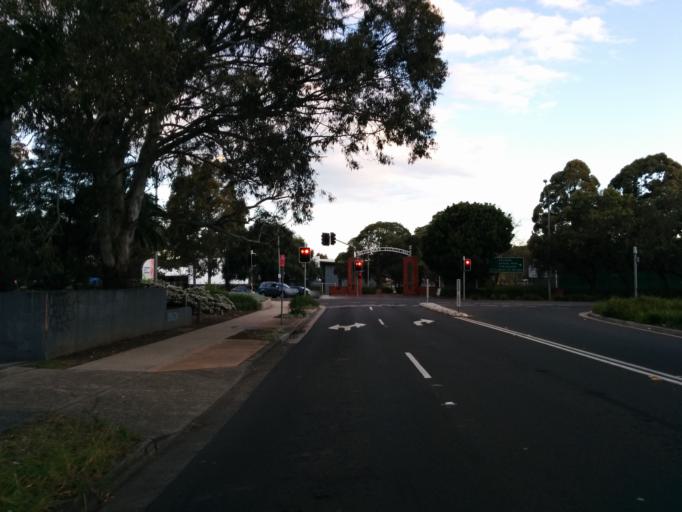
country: AU
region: New South Wales
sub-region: Fairfield
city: Carramar
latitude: -33.8737
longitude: 150.9593
